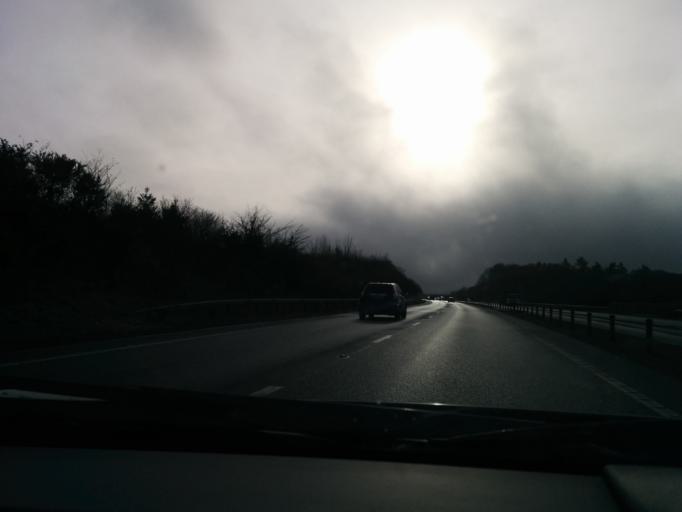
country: GB
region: England
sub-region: West Berkshire
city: Newbury
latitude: 51.3817
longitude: -1.3631
